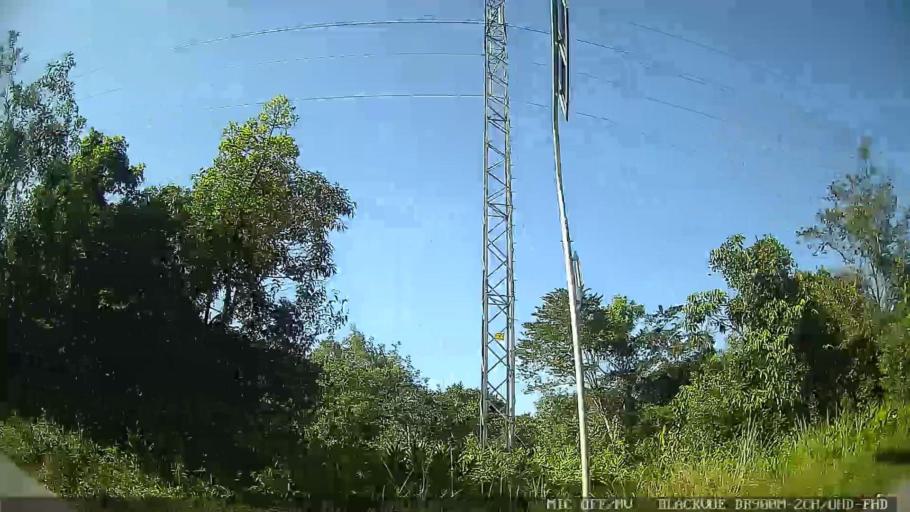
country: BR
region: Sao Paulo
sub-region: Santos
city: Santos
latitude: -23.9011
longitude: -46.3043
